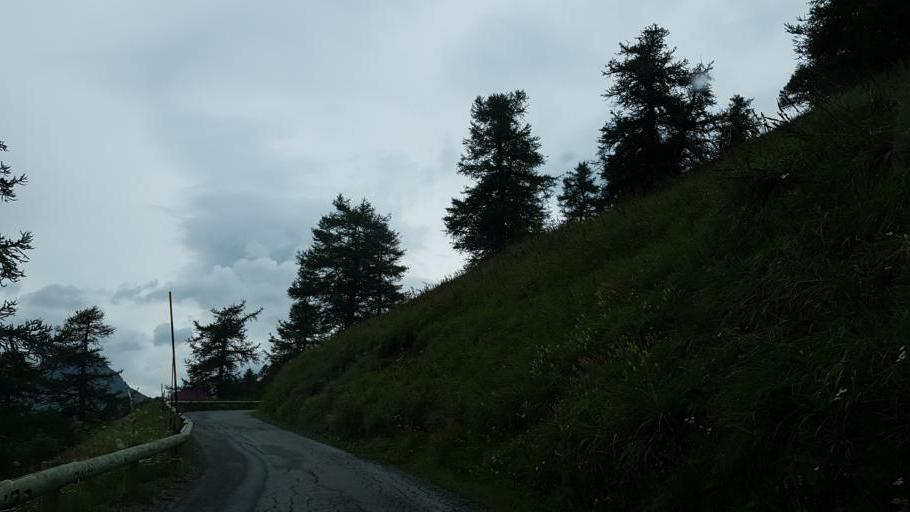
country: IT
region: Piedmont
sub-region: Provincia di Cuneo
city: Serre
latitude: 44.5239
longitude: 7.1044
